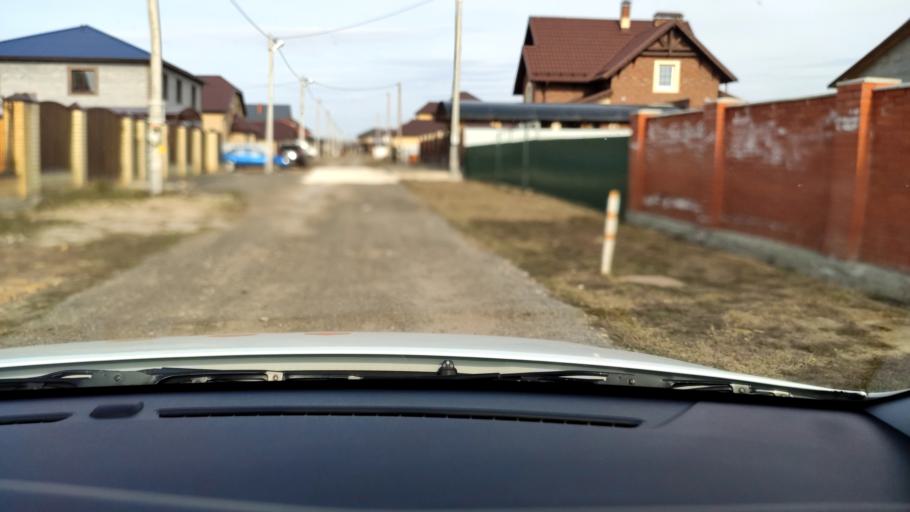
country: RU
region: Tatarstan
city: Stolbishchi
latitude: 55.6427
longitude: 49.3171
